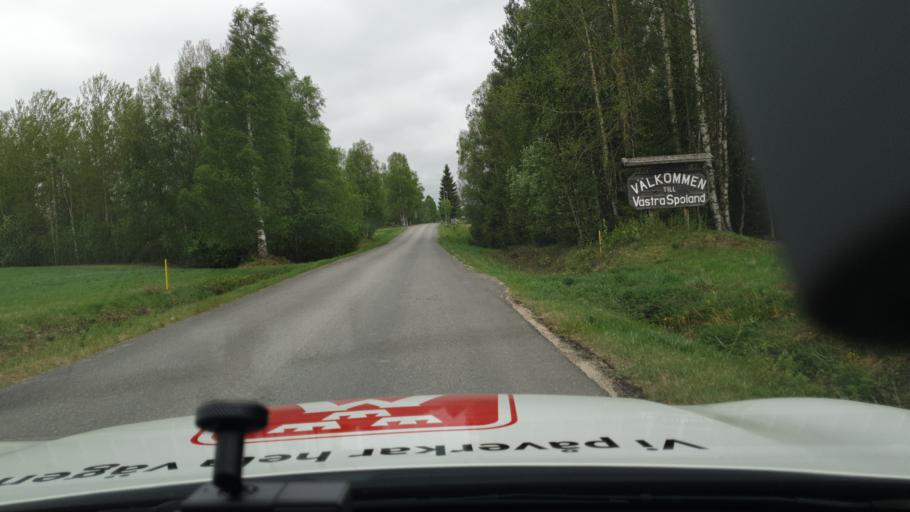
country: SE
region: Vaesterbotten
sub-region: Vannas Kommun
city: Vannasby
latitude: 63.9568
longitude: 19.8696
